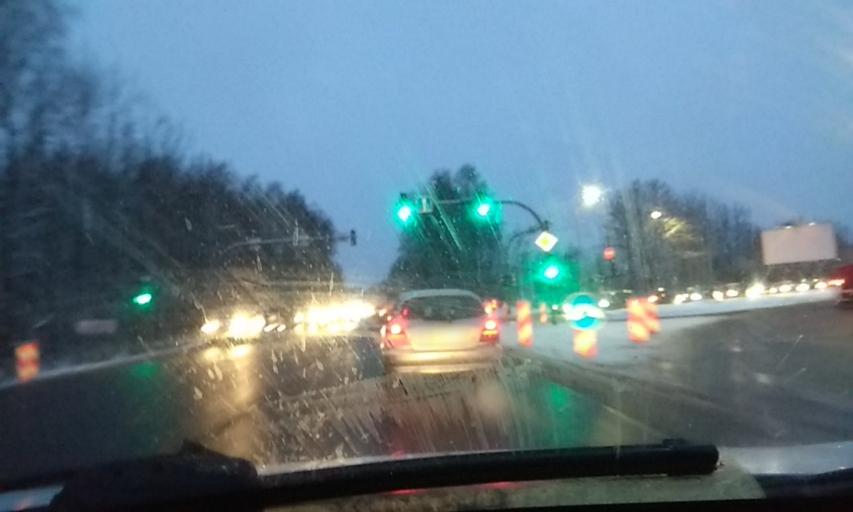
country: LT
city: Ramuciai
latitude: 54.9180
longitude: 24.0410
